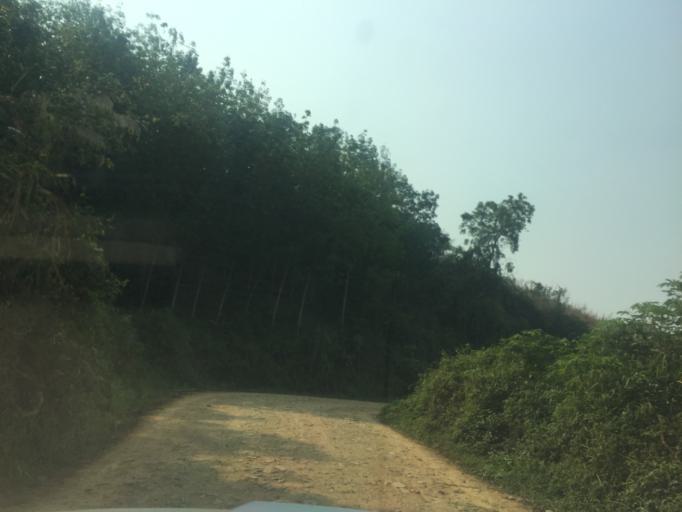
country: TH
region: Phayao
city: Phu Sang
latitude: 19.6513
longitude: 100.5272
